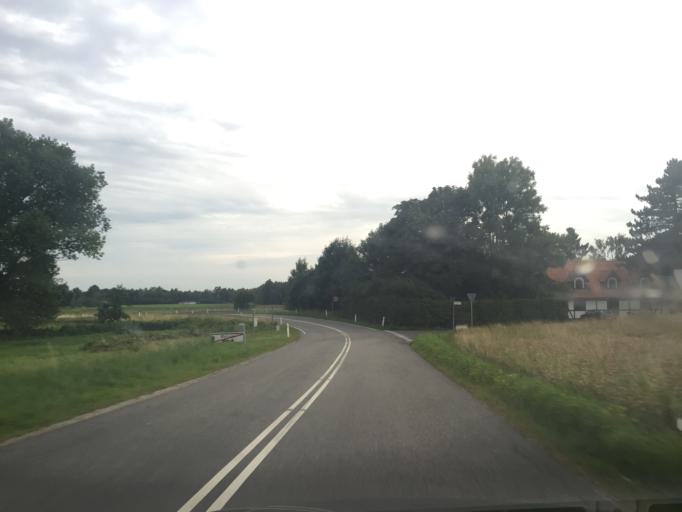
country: DK
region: Capital Region
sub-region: Egedal Kommune
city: Stenlose
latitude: 55.7287
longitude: 12.2044
